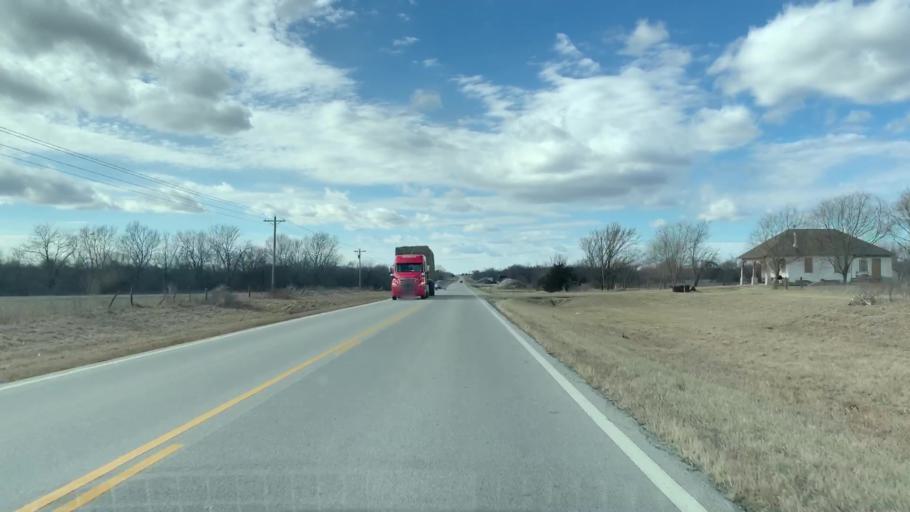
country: US
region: Kansas
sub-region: Neosho County
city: Erie
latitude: 37.5292
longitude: -95.2822
